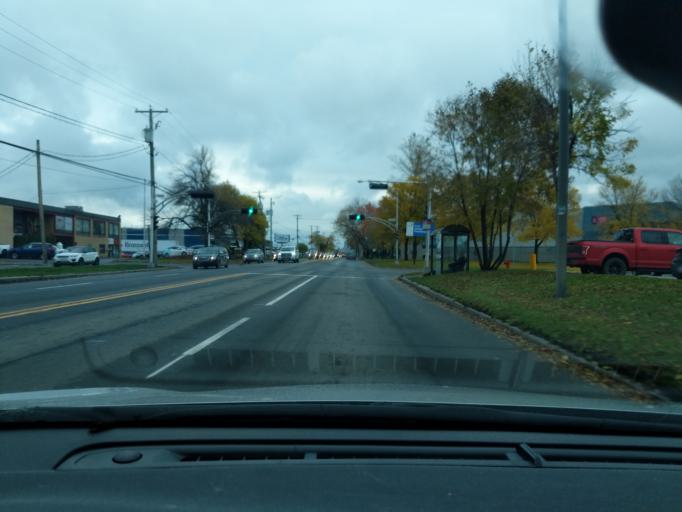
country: CA
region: Quebec
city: L'Ancienne-Lorette
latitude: 46.8062
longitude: -71.3051
